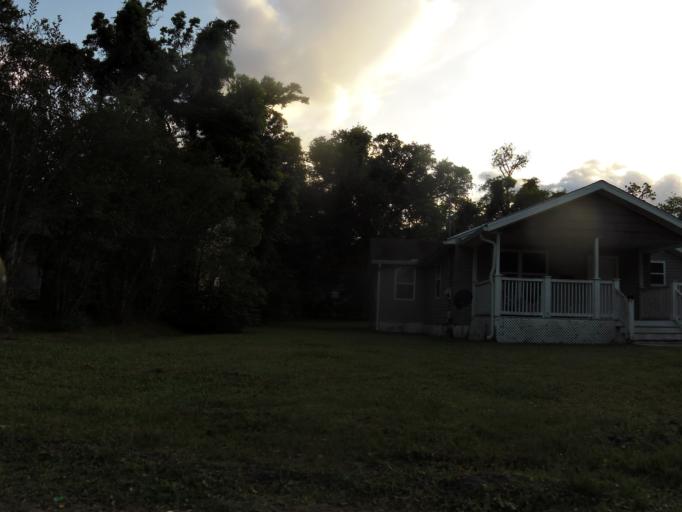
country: US
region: Florida
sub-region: Duval County
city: Jacksonville
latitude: 30.3026
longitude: -81.6238
